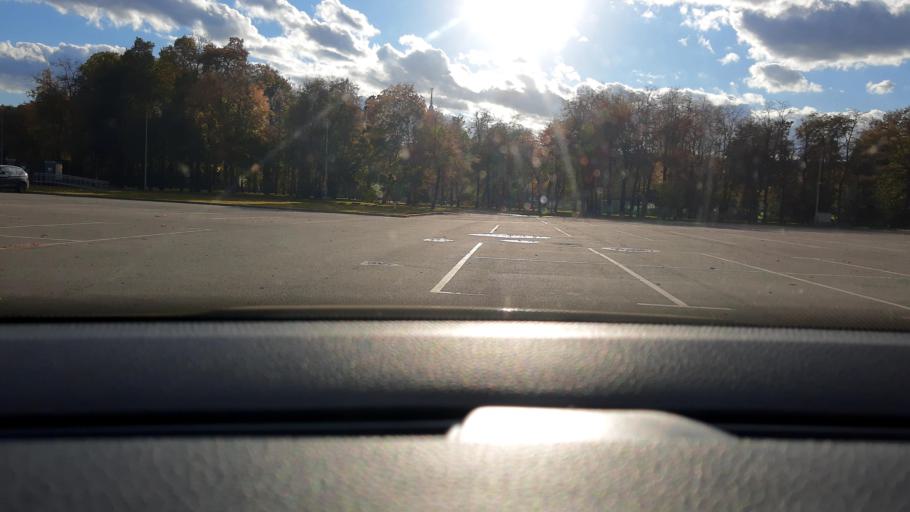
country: RU
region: Moscow
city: Luzhniki
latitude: 55.7176
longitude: 37.5510
